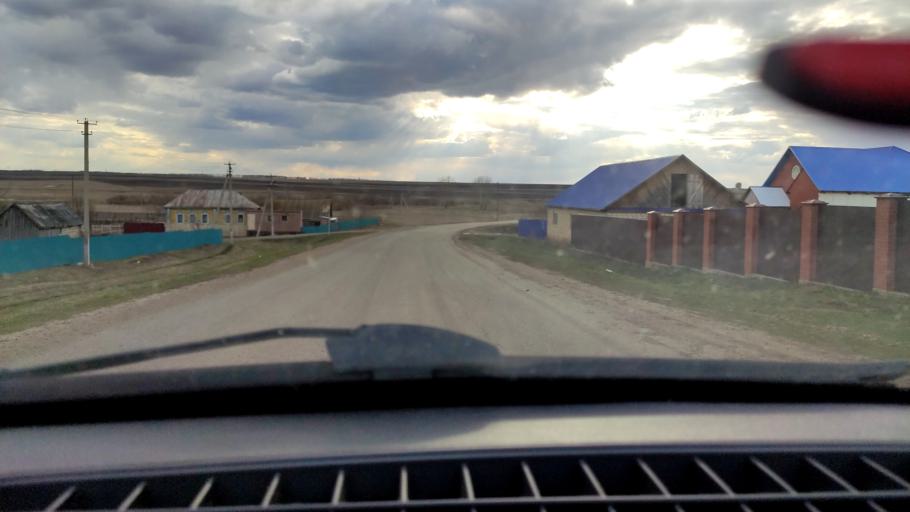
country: RU
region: Bashkortostan
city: Tolbazy
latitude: 54.2912
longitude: 55.9032
